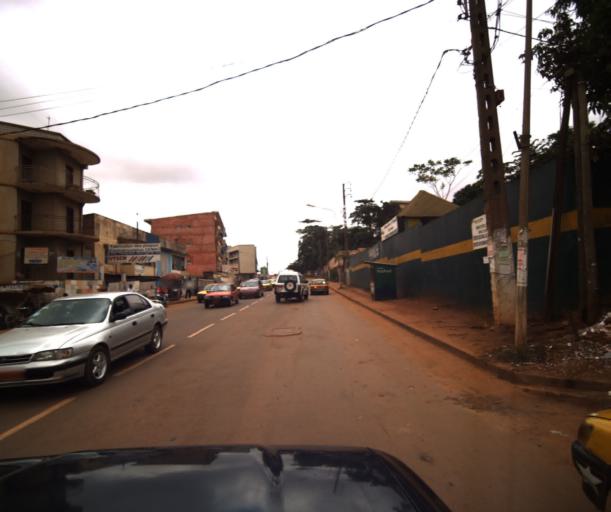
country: CM
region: Centre
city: Yaounde
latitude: 3.8459
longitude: 11.5190
